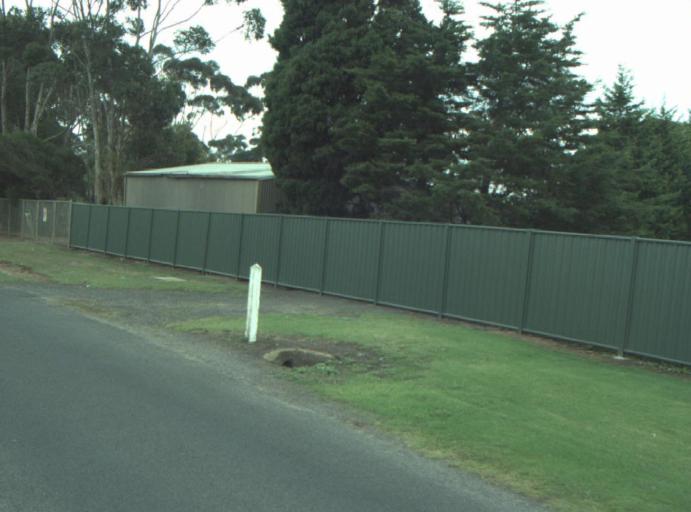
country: AU
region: Victoria
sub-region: Greater Geelong
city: Breakwater
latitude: -38.1749
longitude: 144.3704
